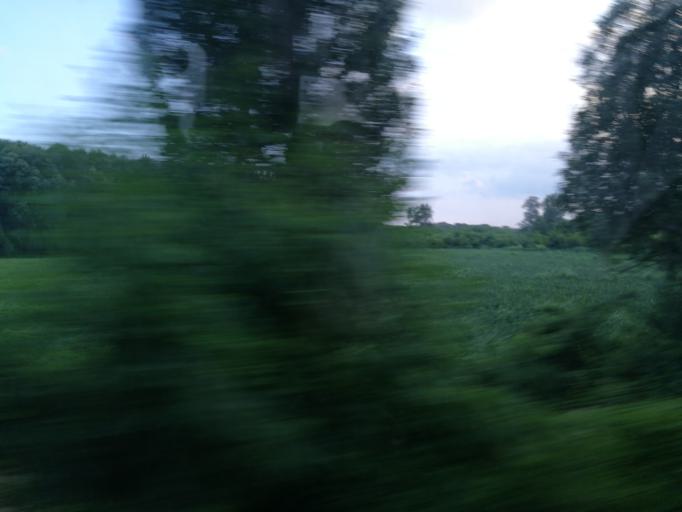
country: RO
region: Dambovita
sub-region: Comuna Contesti
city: Contesti
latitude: 44.6580
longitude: 25.6443
